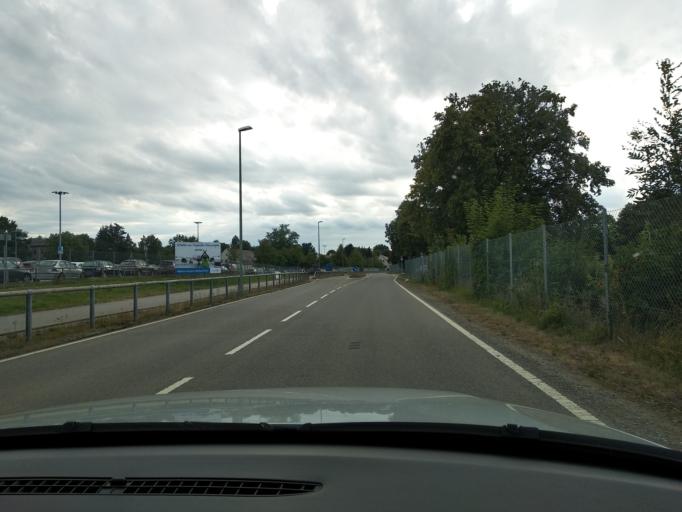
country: DE
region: Bavaria
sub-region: Swabia
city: Memmingerberg
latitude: 47.9917
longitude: 10.2288
